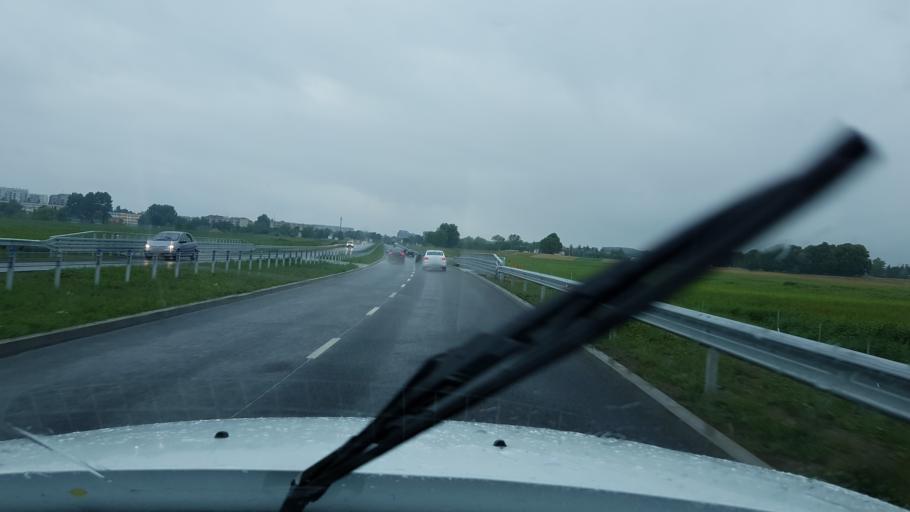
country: PL
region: West Pomeranian Voivodeship
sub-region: Powiat kolobrzeski
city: Kolobrzeg
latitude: 54.1658
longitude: 15.5837
